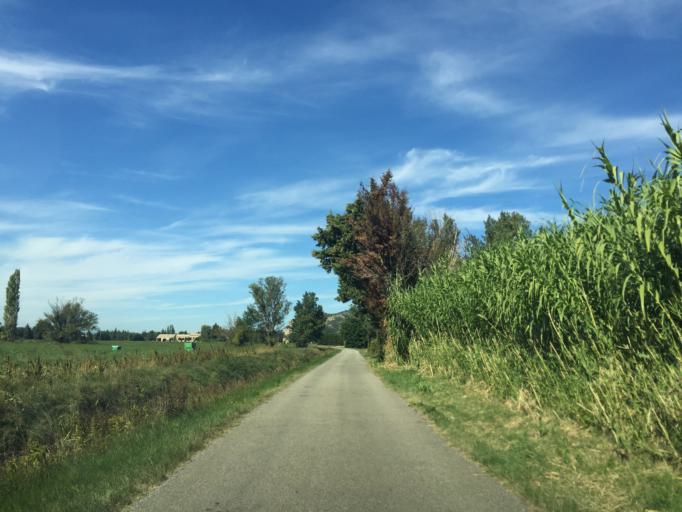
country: FR
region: Provence-Alpes-Cote d'Azur
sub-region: Departement du Vaucluse
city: Mornas
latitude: 44.1845
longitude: 4.7340
